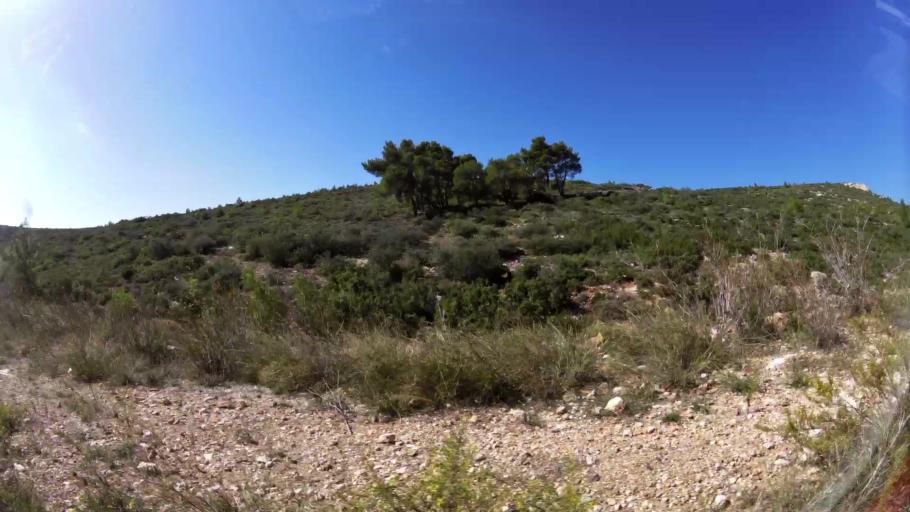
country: GR
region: Attica
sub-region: Nomarchia Anatolikis Attikis
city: Dioni
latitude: 38.0322
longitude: 23.9211
